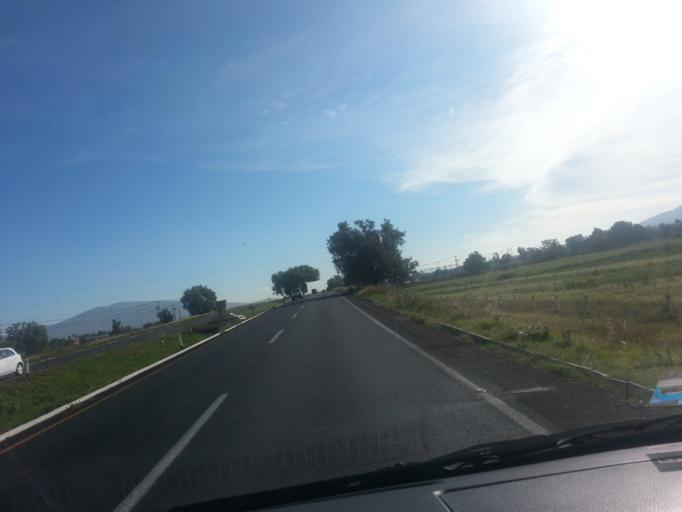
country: MX
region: Mexico
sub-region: Acolman de Nezahualcoyotl
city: San Pedro Tepetitlan
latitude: 19.6410
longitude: -98.8975
